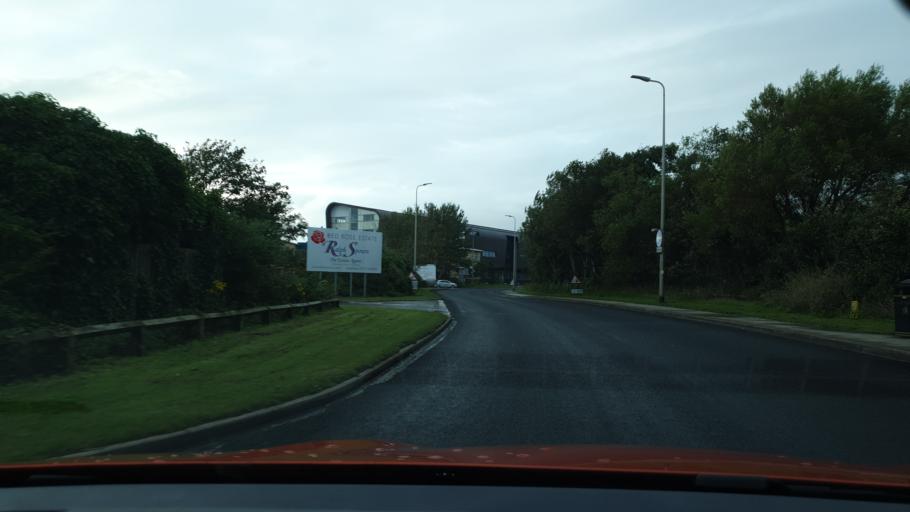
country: GB
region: England
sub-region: Cumbria
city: Barrow in Furness
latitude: 54.1148
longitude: -3.2401
